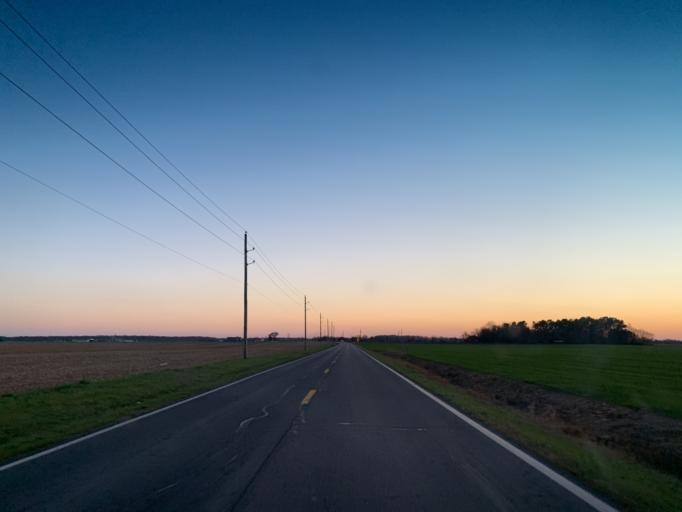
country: US
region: Delaware
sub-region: New Castle County
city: Middletown
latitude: 39.4133
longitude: -75.7469
